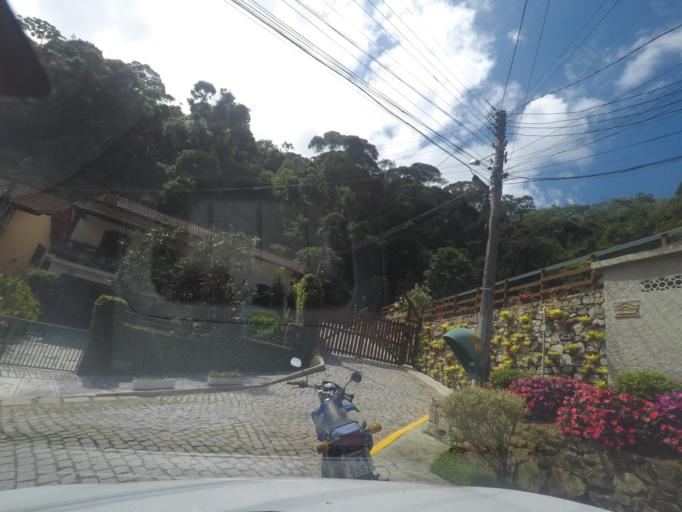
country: BR
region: Rio de Janeiro
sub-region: Teresopolis
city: Teresopolis
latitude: -22.3980
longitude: -42.9880
